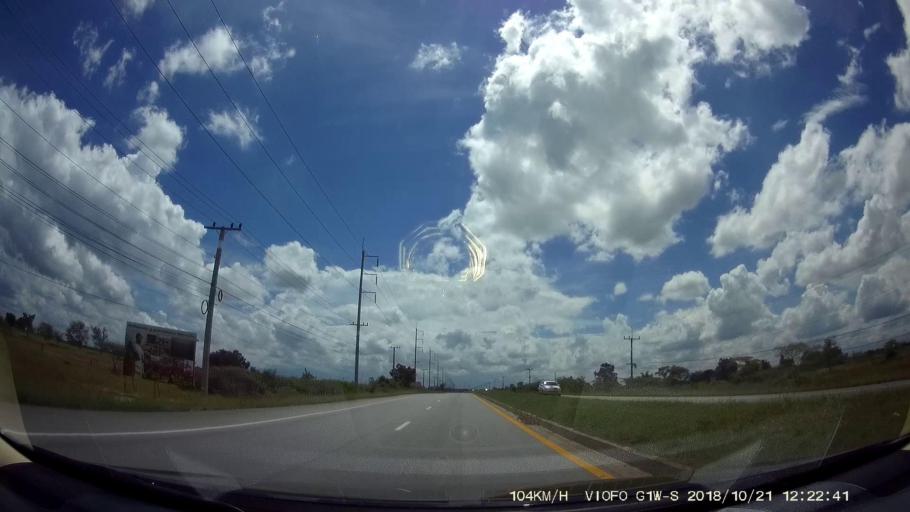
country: TH
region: Nakhon Ratchasima
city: Dan Khun Thot
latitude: 15.2572
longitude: 101.7893
